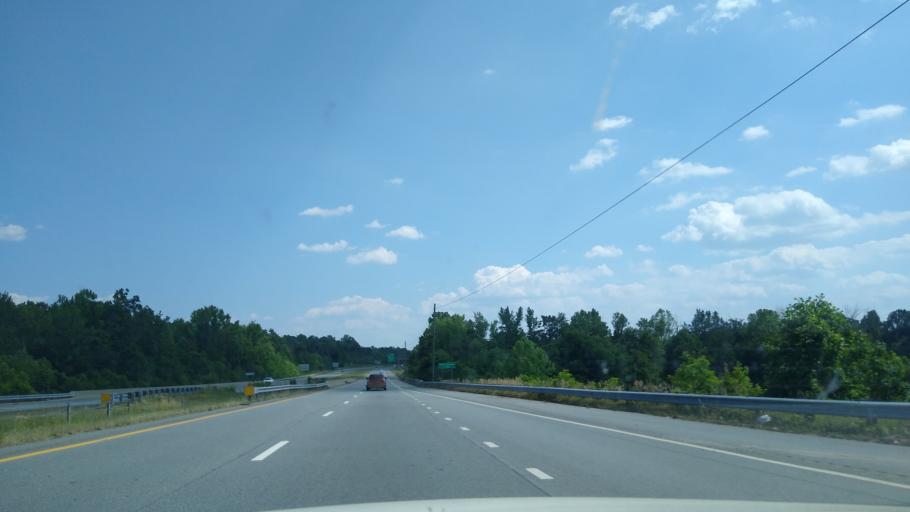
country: US
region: North Carolina
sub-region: Guilford County
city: McLeansville
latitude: 36.0835
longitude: -79.6955
